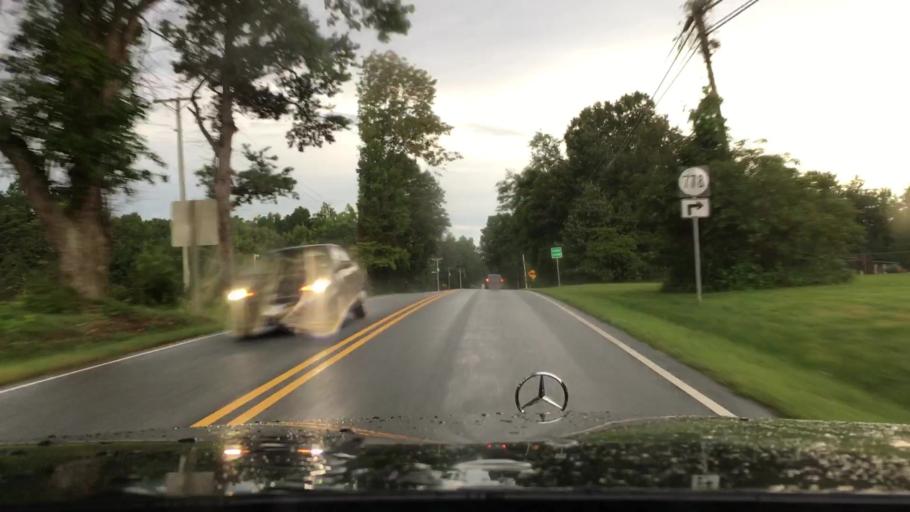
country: US
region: Virginia
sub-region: Amherst County
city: Amherst
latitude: 37.7188
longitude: -79.0184
